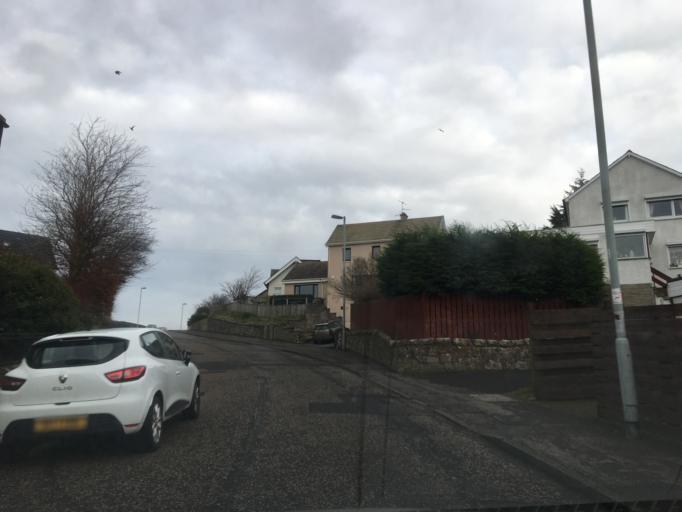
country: GB
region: Scotland
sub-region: Midlothian
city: Penicuik
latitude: 55.8279
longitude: -3.2182
